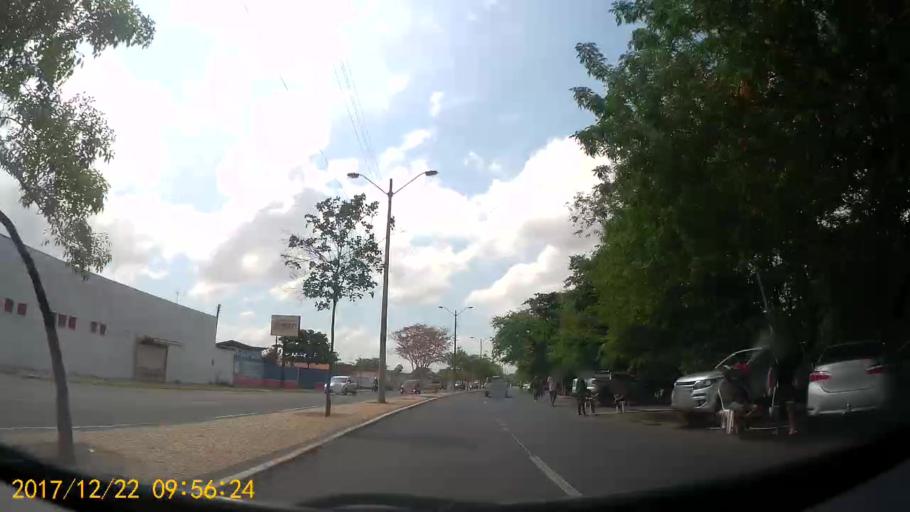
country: BR
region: Piaui
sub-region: Teresina
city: Teresina
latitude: -5.1030
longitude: -42.8147
